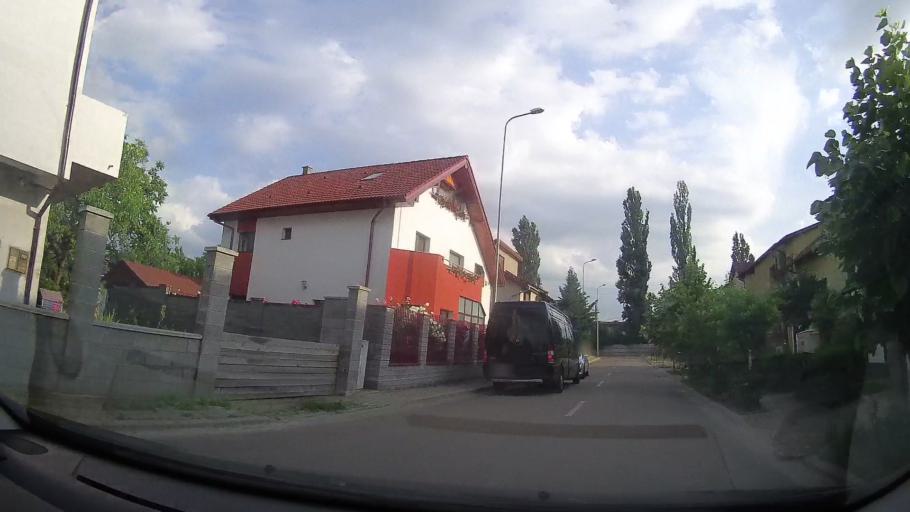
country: RO
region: Timis
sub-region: Comuna Dumbravita
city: Dumbravita
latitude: 45.7821
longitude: 21.2317
